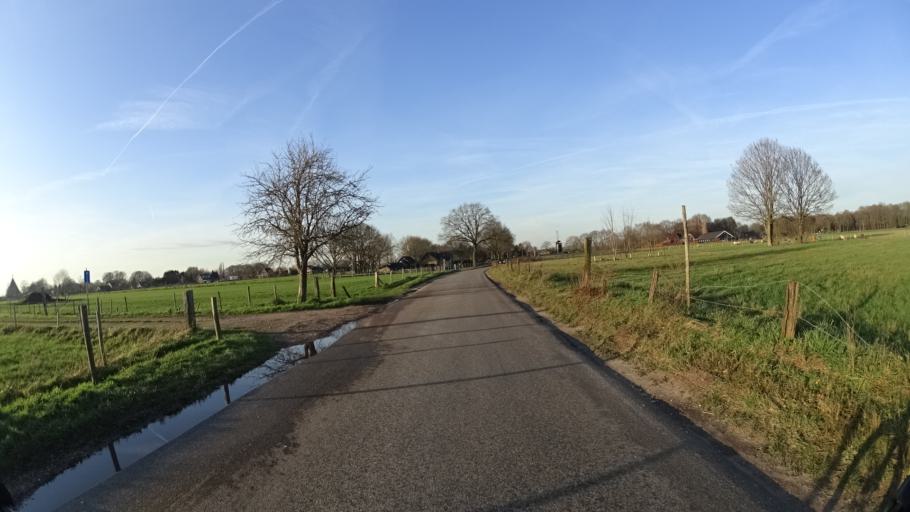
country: NL
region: Gelderland
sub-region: Gemeente Ede
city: Ede
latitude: 52.0588
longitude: 5.6509
